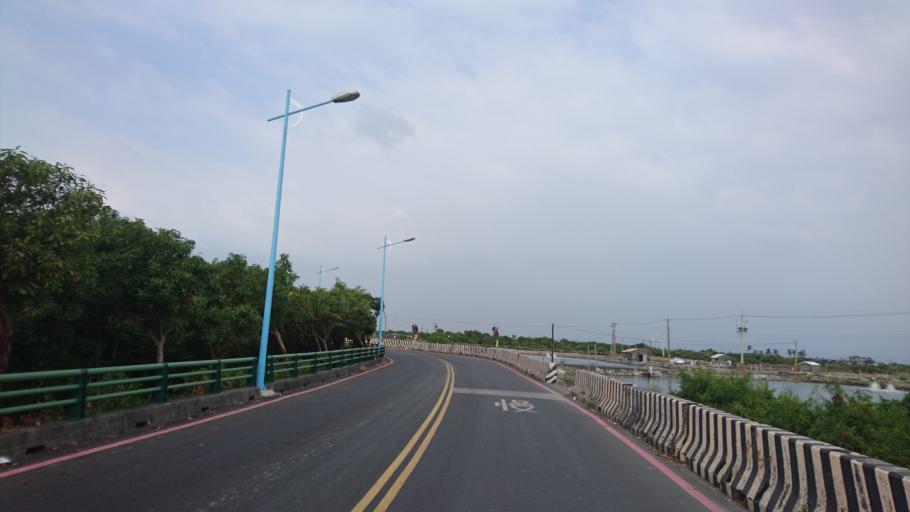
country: TW
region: Taiwan
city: Fengshan
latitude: 22.4318
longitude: 120.4915
